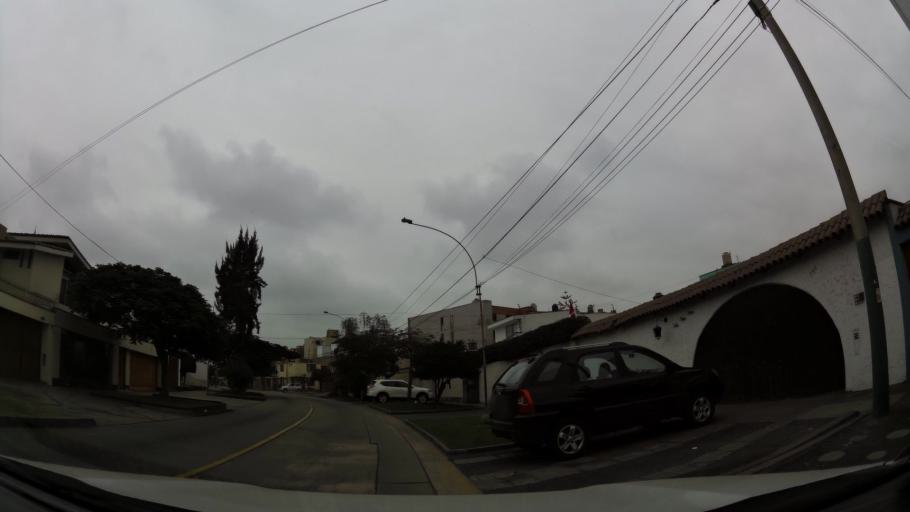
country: PE
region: Lima
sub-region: Lima
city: San Luis
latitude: -12.0999
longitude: -76.9987
